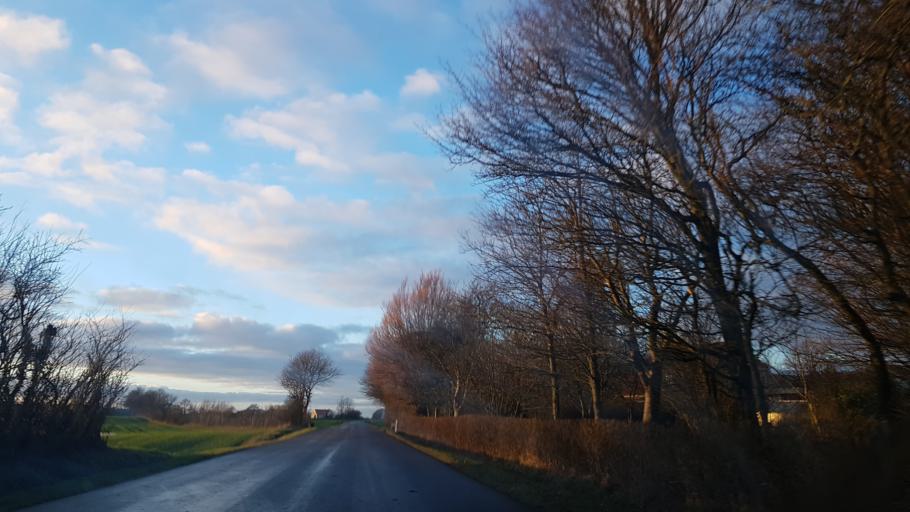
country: DK
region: South Denmark
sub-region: Kolding Kommune
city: Vamdrup
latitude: 55.3673
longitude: 9.3167
